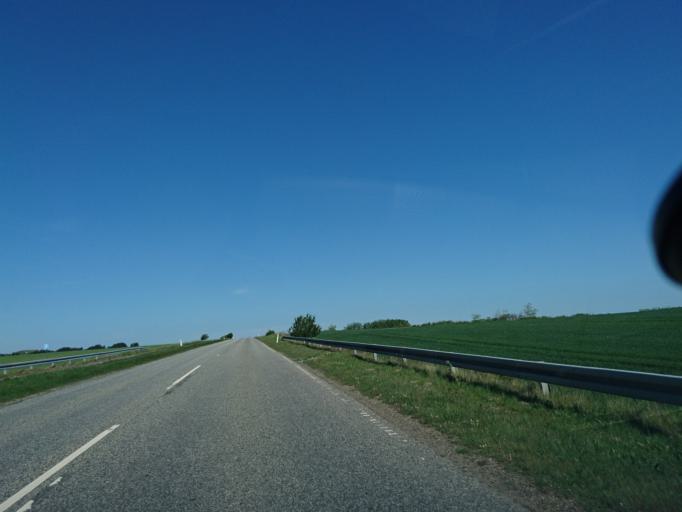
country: DK
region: North Denmark
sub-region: Hjorring Kommune
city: Hjorring
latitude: 57.4988
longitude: 10.0039
